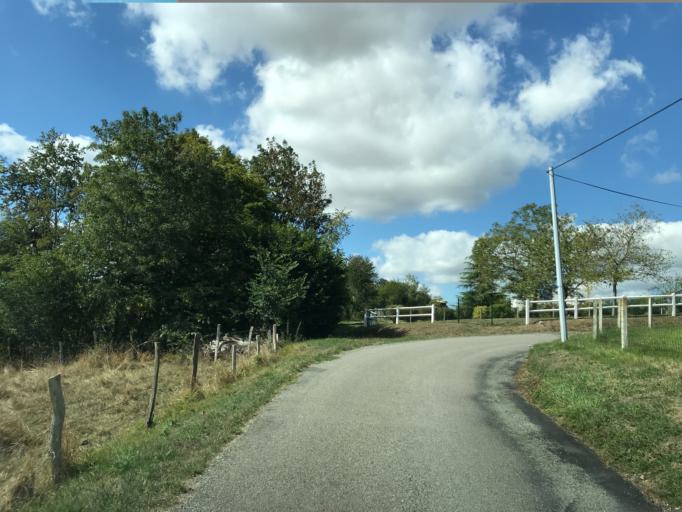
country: FR
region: Haute-Normandie
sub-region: Departement de l'Eure
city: La Chapelle-Reanville
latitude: 49.1140
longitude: 1.3750
